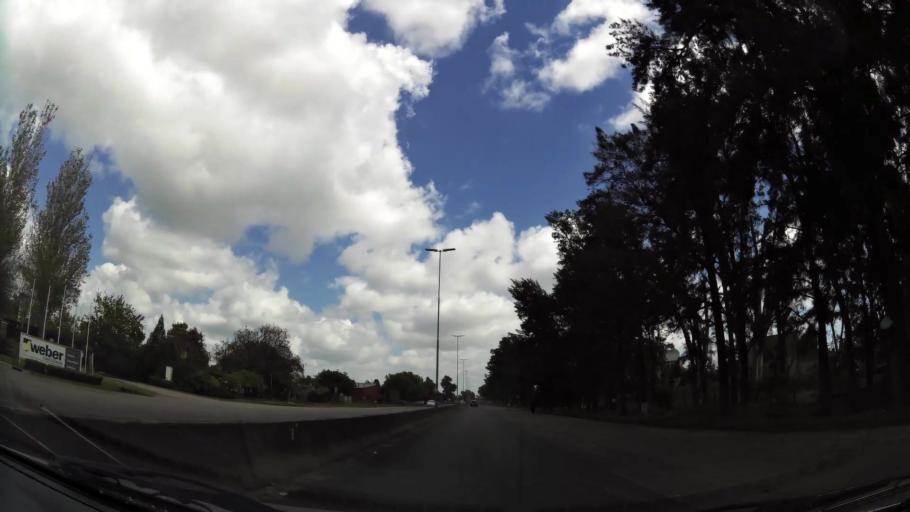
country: AR
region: Buenos Aires
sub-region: Partido de Quilmes
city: Quilmes
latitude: -34.8279
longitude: -58.2198
